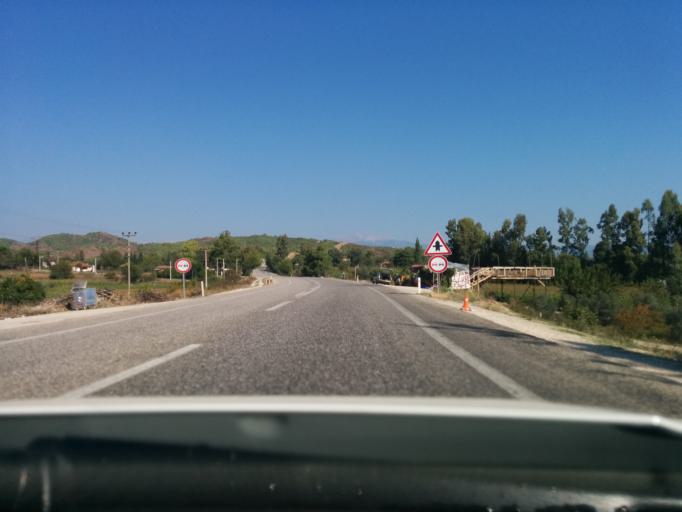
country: TR
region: Mugla
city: Kemer
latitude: 36.5914
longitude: 29.3508
